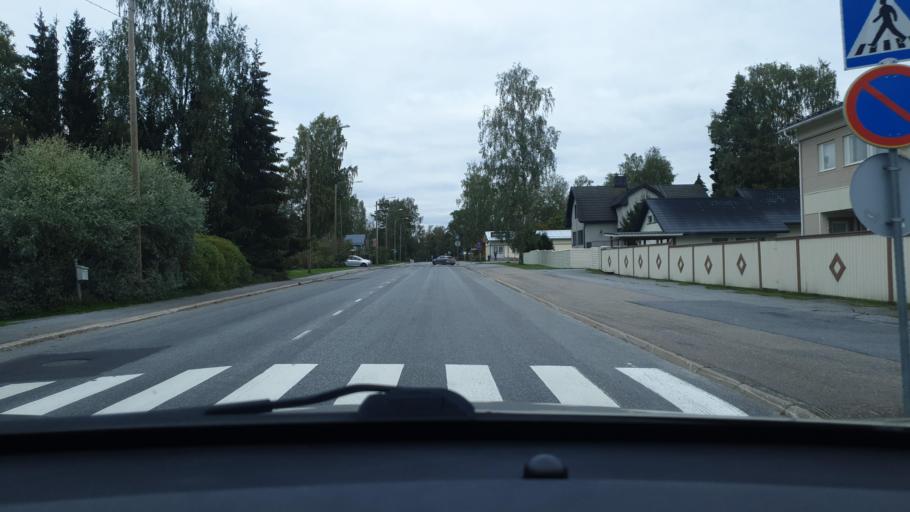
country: FI
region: Ostrobothnia
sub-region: Vaasa
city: Korsholm
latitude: 63.0944
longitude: 21.6658
